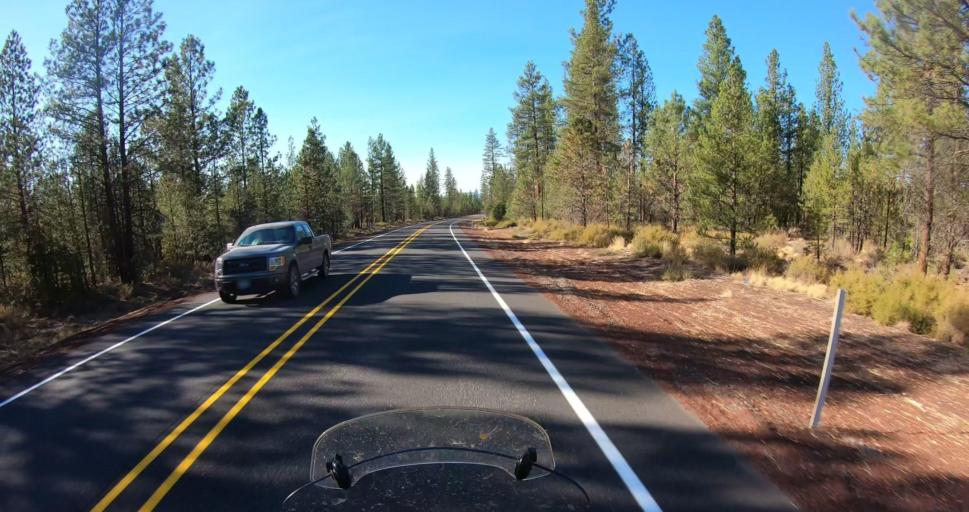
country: US
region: Oregon
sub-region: Deschutes County
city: La Pine
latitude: 43.4926
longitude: -121.4418
